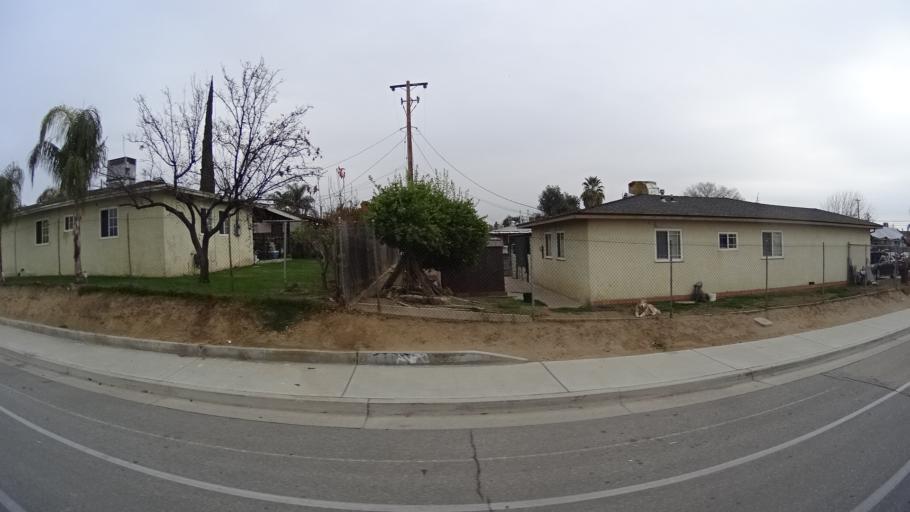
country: US
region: California
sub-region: Kern County
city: Bakersfield
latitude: 35.3698
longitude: -118.9496
